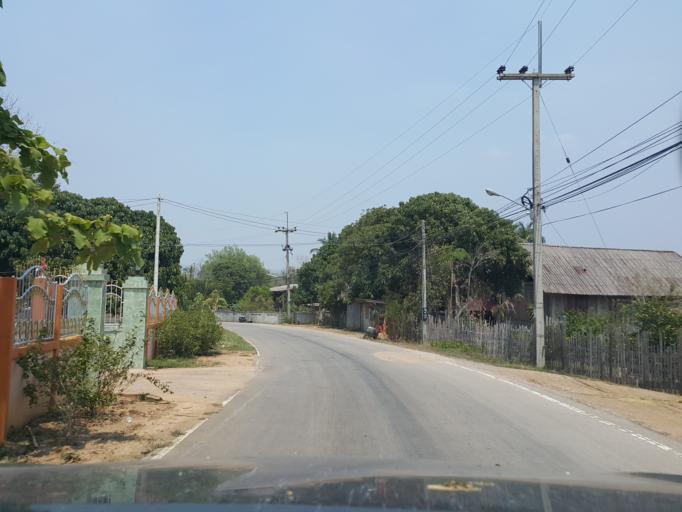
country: TH
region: Lampang
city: Mae Phrik
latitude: 17.5322
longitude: 99.1475
